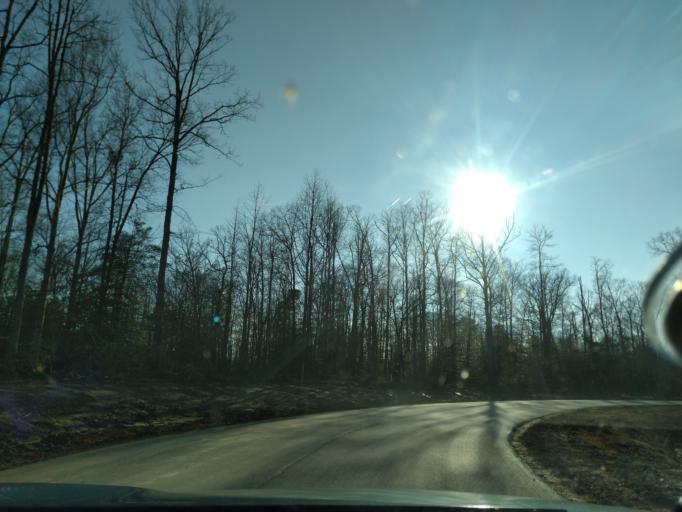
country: US
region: Maryland
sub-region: Charles County
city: La Plata
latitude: 38.4903
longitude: -76.8883
